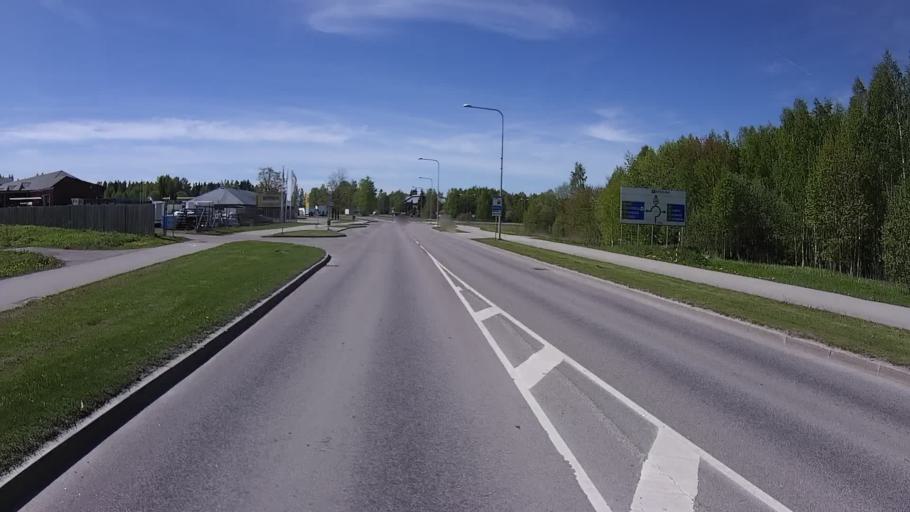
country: EE
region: Polvamaa
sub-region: Polva linn
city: Polva
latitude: 58.0684
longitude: 27.0764
